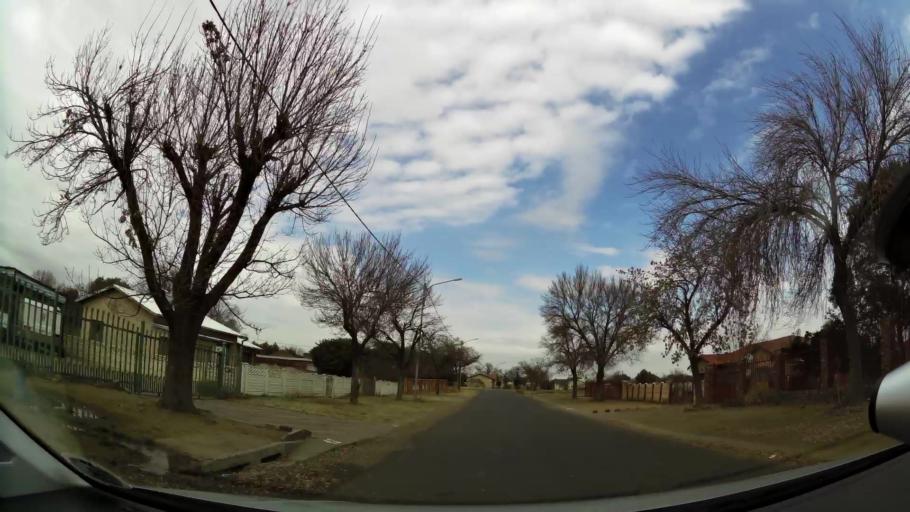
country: ZA
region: Orange Free State
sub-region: Fezile Dabi District Municipality
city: Kroonstad
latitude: -27.6417
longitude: 27.2291
